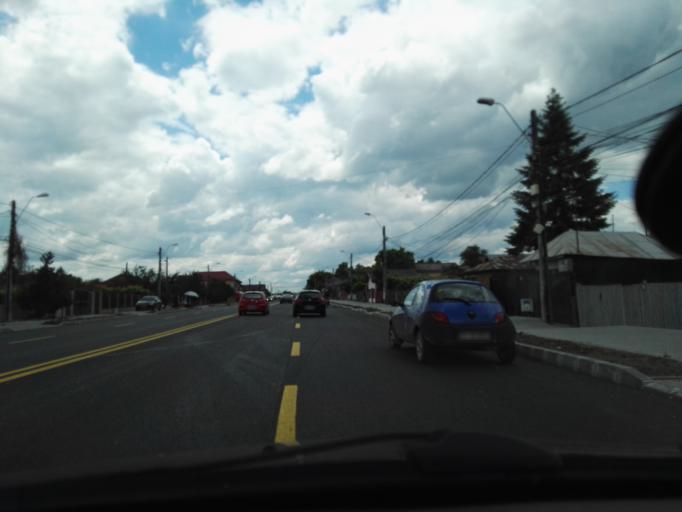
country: RO
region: Ilfov
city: Prim Decembrie
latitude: 44.2871
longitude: 26.0602
